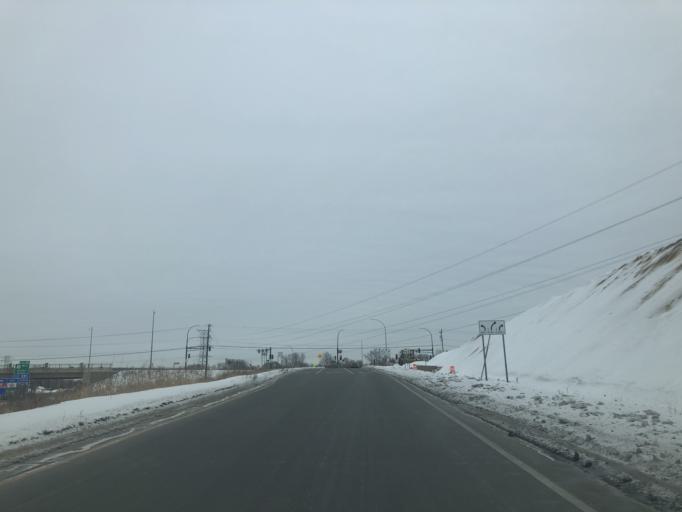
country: US
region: Minnesota
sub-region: Ramsey County
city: New Brighton
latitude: 45.0775
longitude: -93.1848
